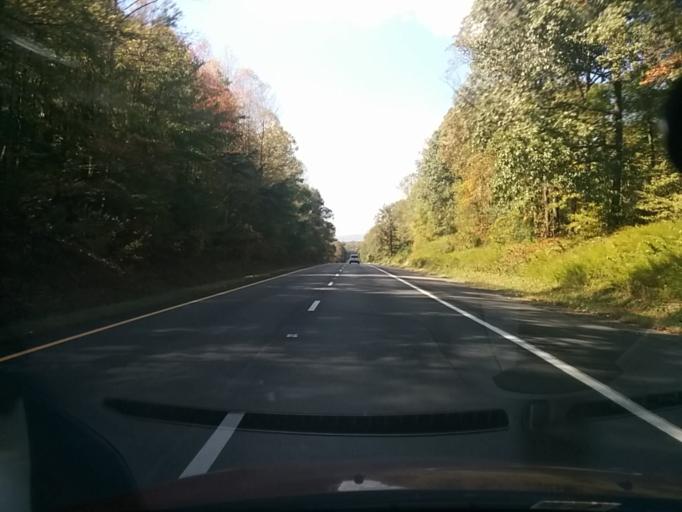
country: US
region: Virginia
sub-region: Albemarle County
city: Crozet
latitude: 38.0308
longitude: -78.6649
